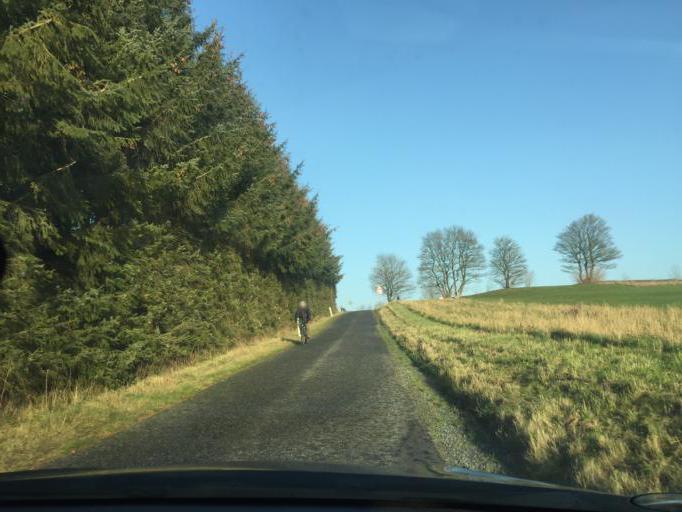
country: DK
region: South Denmark
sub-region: Faaborg-Midtfyn Kommune
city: Faaborg
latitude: 55.1344
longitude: 10.2476
